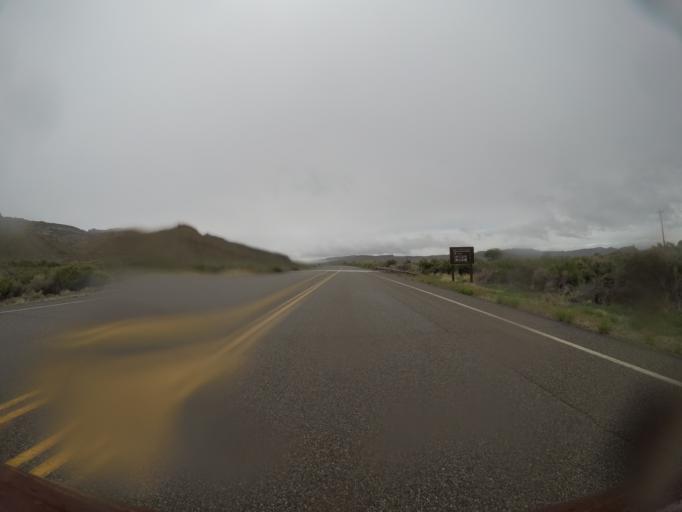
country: US
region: Wyoming
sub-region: Big Horn County
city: Lovell
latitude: 44.9602
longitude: -108.2871
